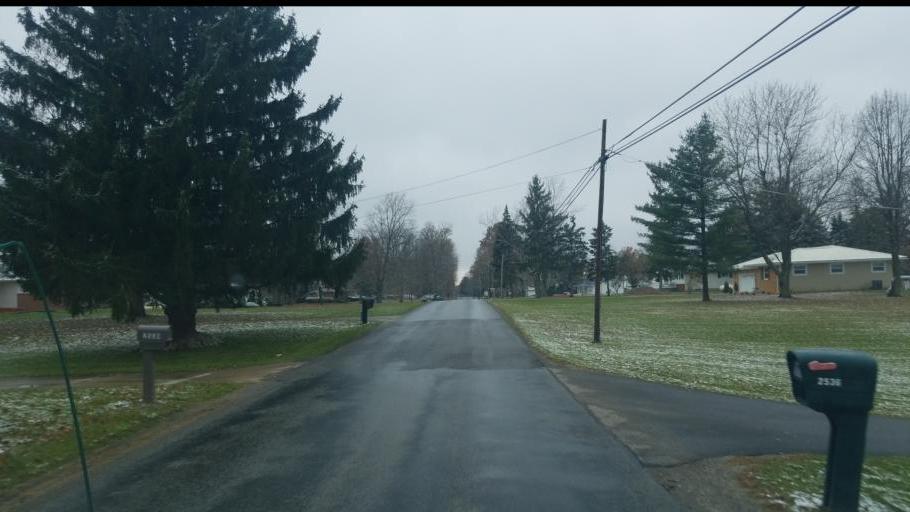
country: US
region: Ohio
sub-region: Richland County
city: Shelby
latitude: 40.8723
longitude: -82.6065
